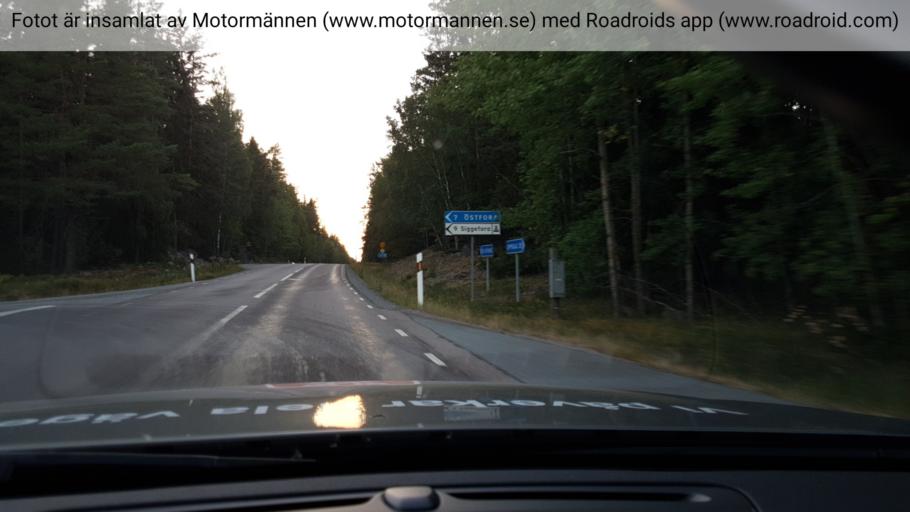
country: SE
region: Uppsala
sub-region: Heby Kommun
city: OEstervala
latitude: 60.0005
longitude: 17.3064
